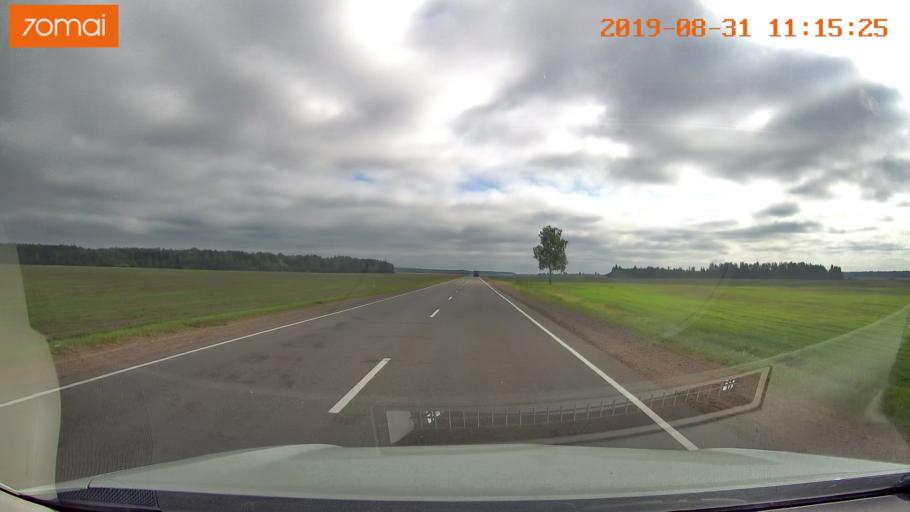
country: BY
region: Mogilev
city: Chavusy
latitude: 53.8099
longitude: 30.8586
